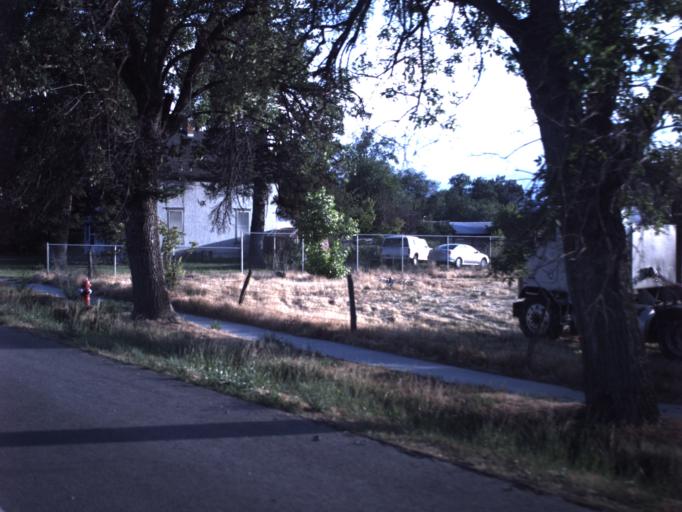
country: US
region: Utah
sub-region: Sanpete County
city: Ephraim
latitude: 39.3669
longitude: -111.5871
